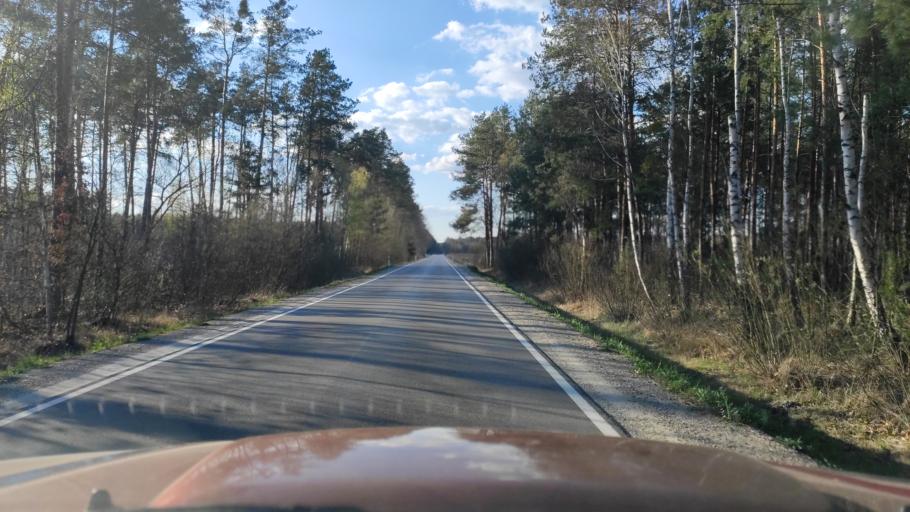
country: PL
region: Masovian Voivodeship
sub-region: Powiat zwolenski
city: Zwolen
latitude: 51.3939
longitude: 21.5455
